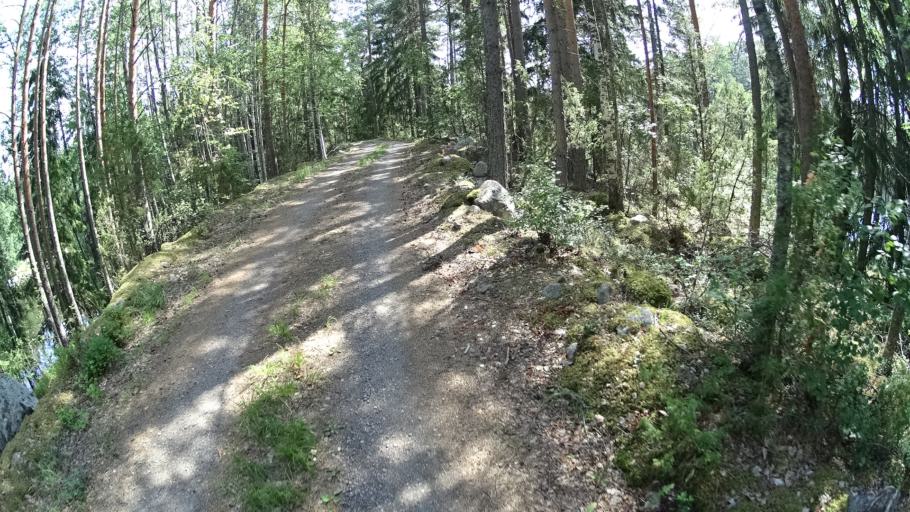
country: FI
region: Haeme
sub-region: Forssa
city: Tammela
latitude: 60.7686
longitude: 23.8781
